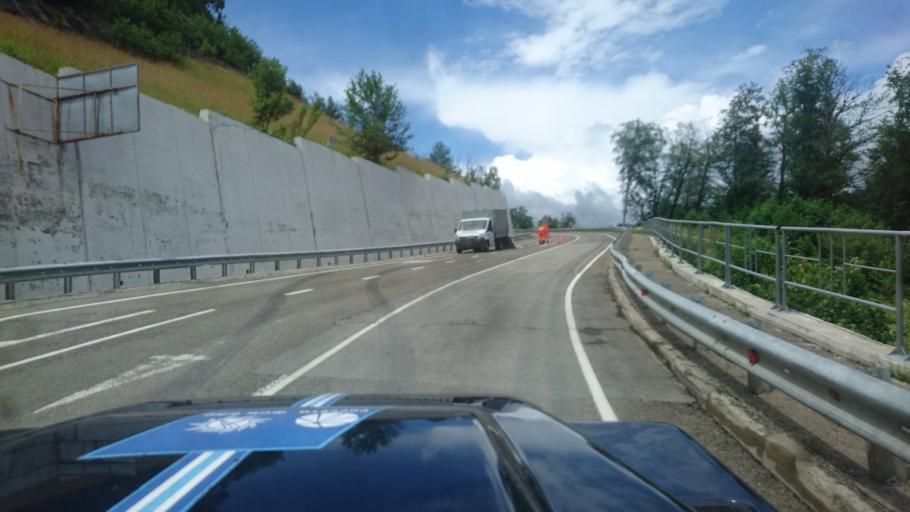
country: RU
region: Krasnodarskiy
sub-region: Sochi City
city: Krasnaya Polyana
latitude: 43.6579
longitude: 40.3272
